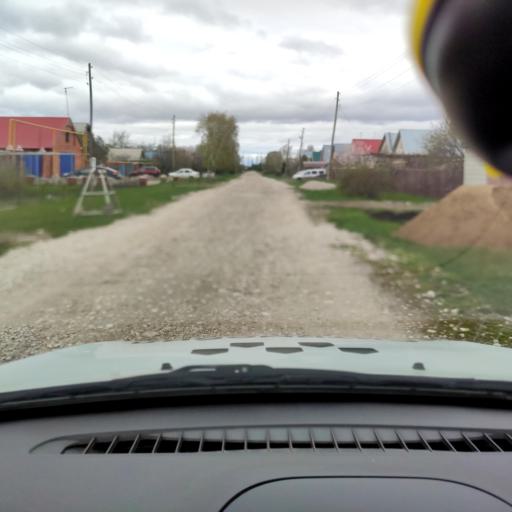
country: RU
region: Samara
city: Tol'yatti
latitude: 53.5800
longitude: 49.3297
